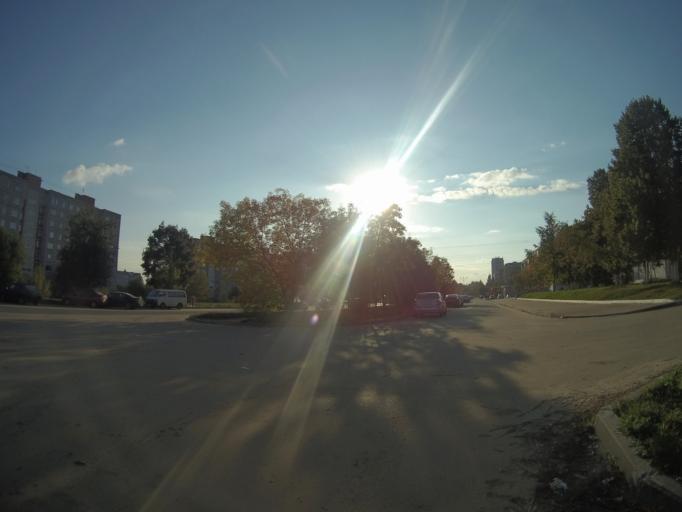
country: RU
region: Vladimir
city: Vladimir
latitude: 56.1099
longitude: 40.3496
